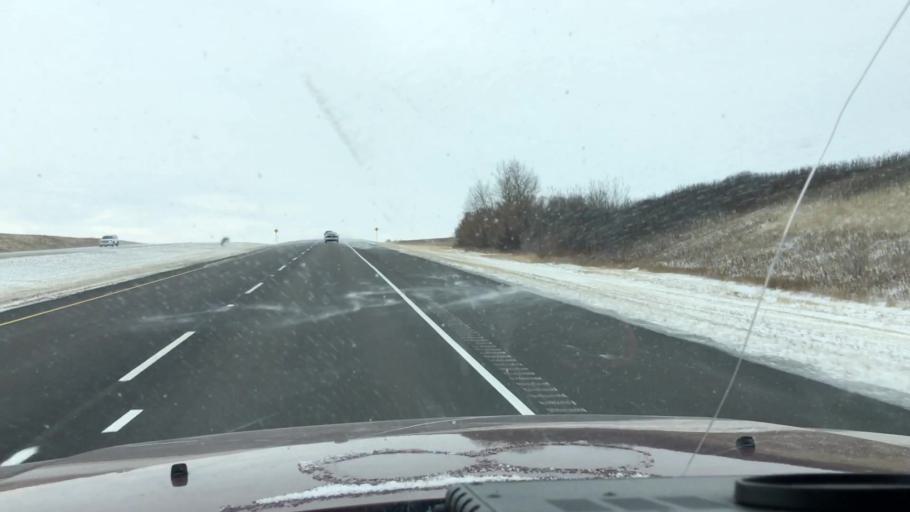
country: CA
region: Saskatchewan
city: Saskatoon
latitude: 51.7243
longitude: -106.4721
